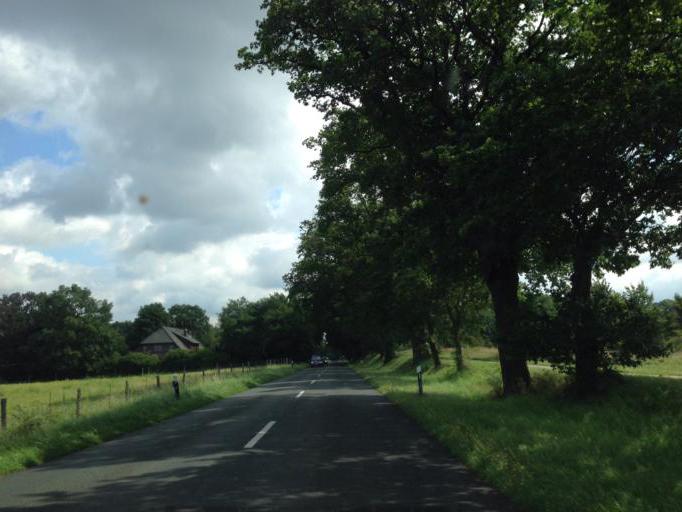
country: DE
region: Lower Saxony
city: Adendorf
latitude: 53.2973
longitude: 10.4446
